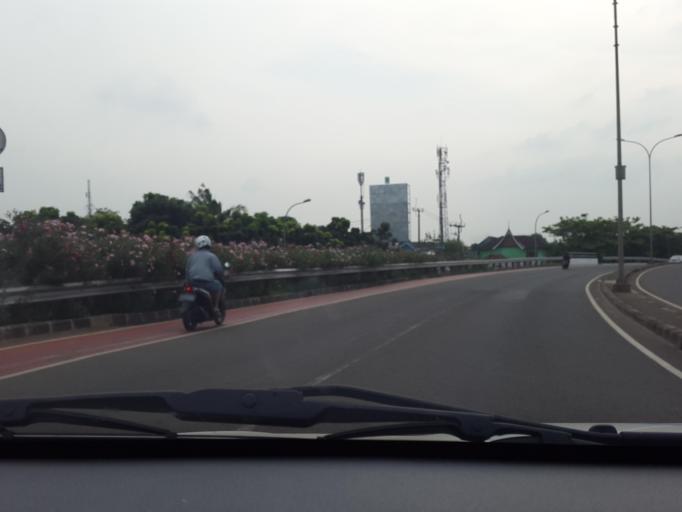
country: ID
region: Banten
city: South Tangerang
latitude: -6.2753
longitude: 106.7069
